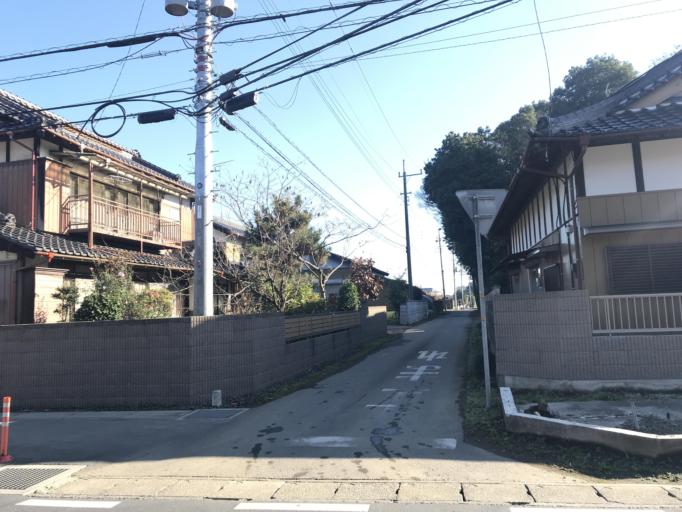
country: JP
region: Tochigi
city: Oyama
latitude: 36.2127
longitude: 139.8230
